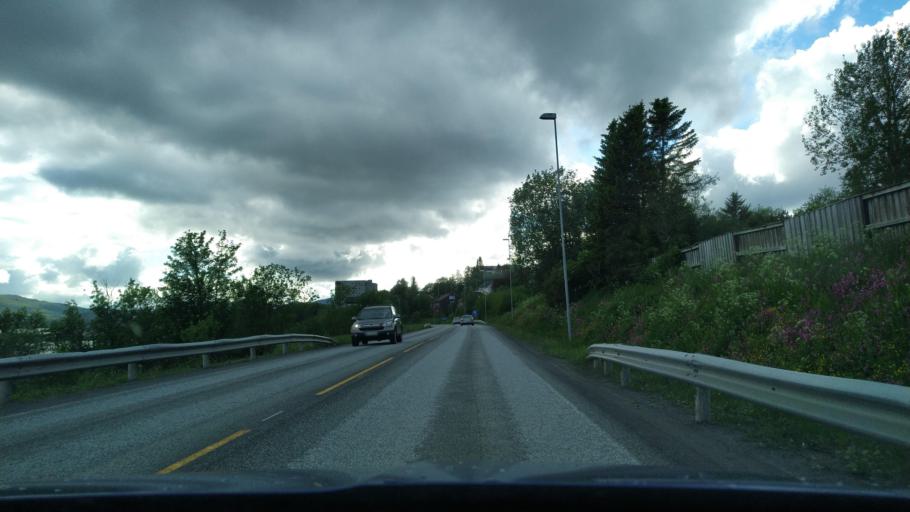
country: NO
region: Troms
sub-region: Lenvik
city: Finnsnes
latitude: 69.2333
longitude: 18.0224
